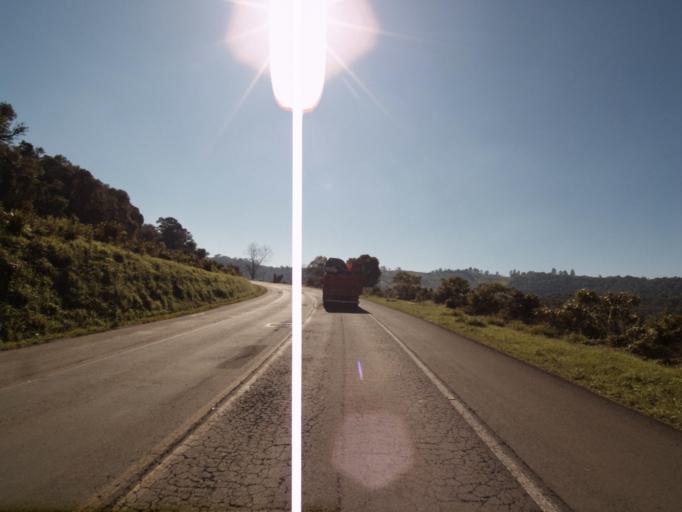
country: BR
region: Rio Grande do Sul
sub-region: Frederico Westphalen
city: Frederico Westphalen
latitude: -27.0649
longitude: -53.2215
